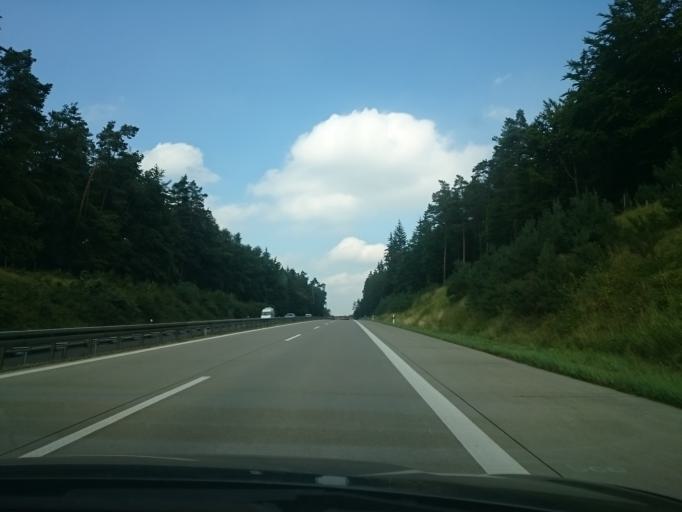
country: DE
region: Brandenburg
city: Althuttendorf
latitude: 53.0568
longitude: 13.8386
